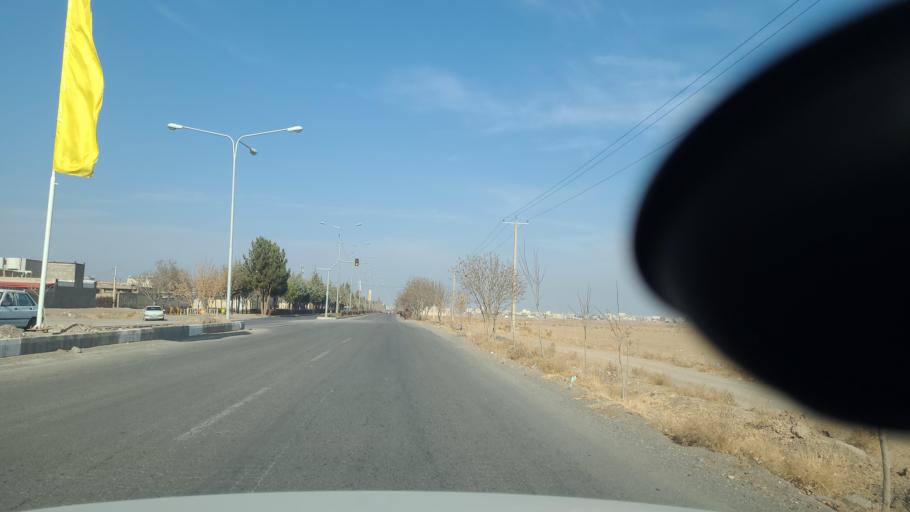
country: IR
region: Razavi Khorasan
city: Fariman
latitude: 35.6805
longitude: 59.8431
